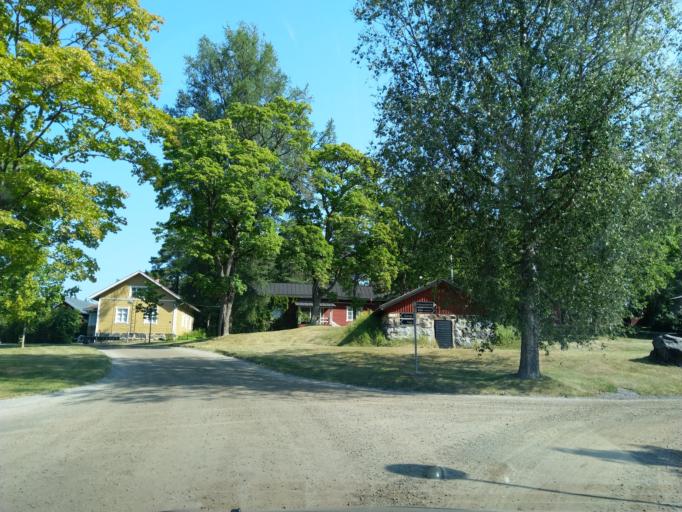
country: FI
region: Satakunta
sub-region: Pori
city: Noormarkku
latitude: 61.5934
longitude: 21.8844
